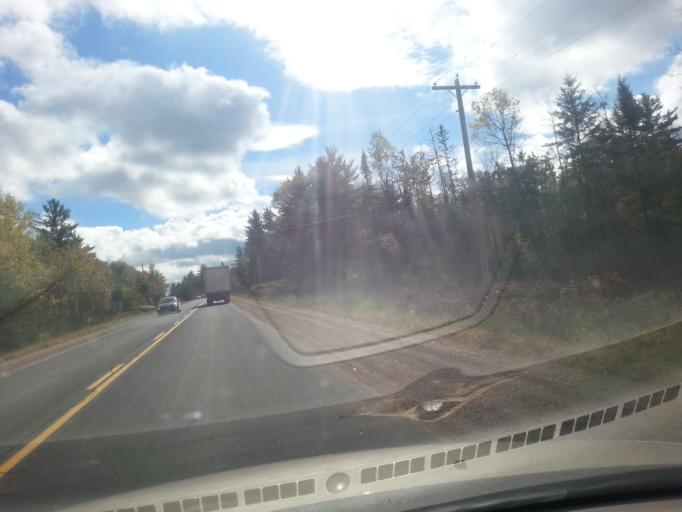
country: CA
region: Ontario
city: Pembroke
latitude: 45.6591
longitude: -77.0863
